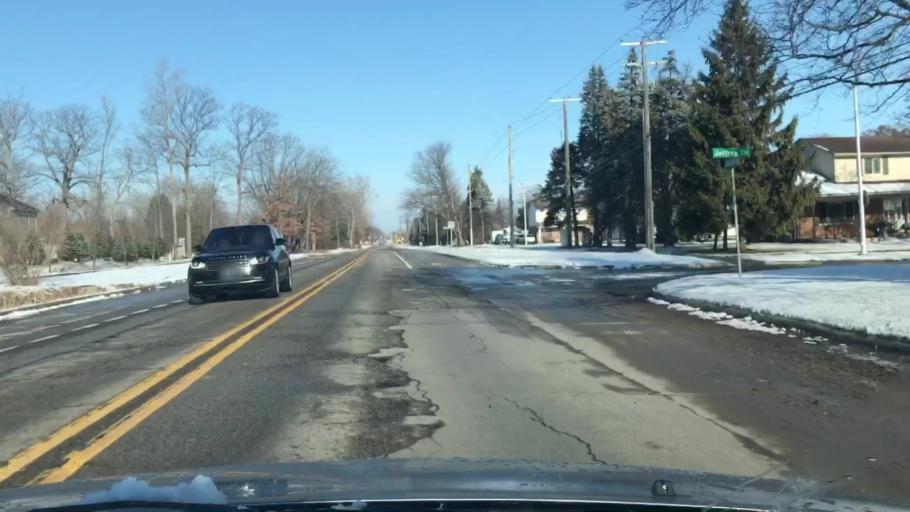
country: US
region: Michigan
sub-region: Oakland County
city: Troy
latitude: 42.6021
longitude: -83.1099
